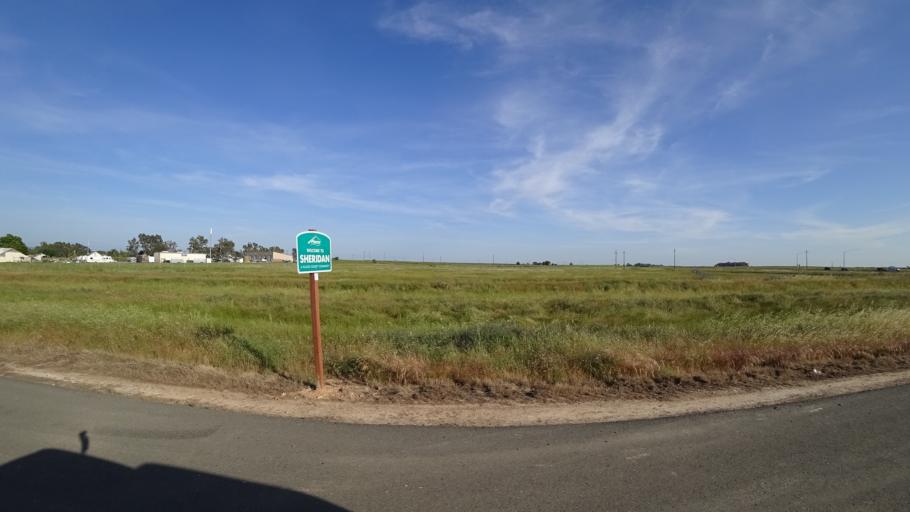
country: US
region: California
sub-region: Placer County
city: Sheridan
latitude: 38.9796
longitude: -121.3807
